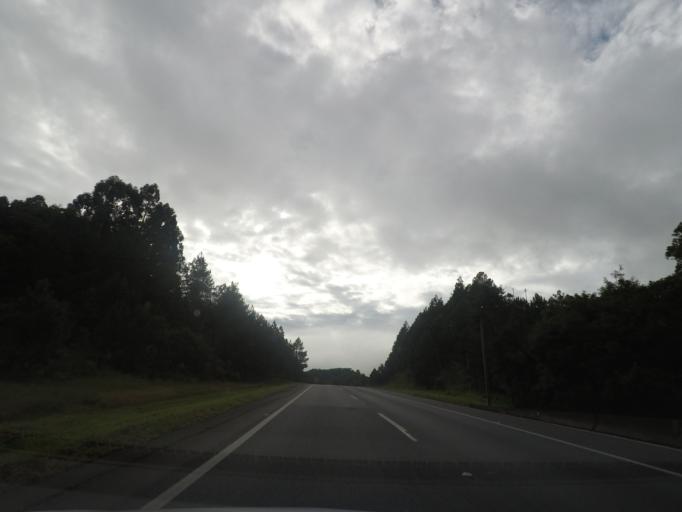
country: BR
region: Parana
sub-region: Campina Grande Do Sul
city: Campina Grande do Sul
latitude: -25.1101
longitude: -48.8399
